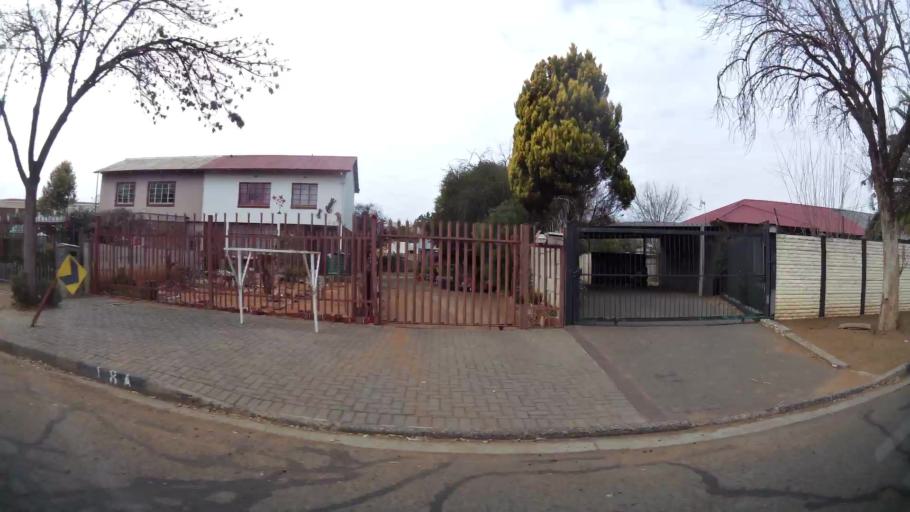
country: ZA
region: Orange Free State
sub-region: Mangaung Metropolitan Municipality
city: Bloemfontein
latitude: -29.1295
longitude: 26.1905
